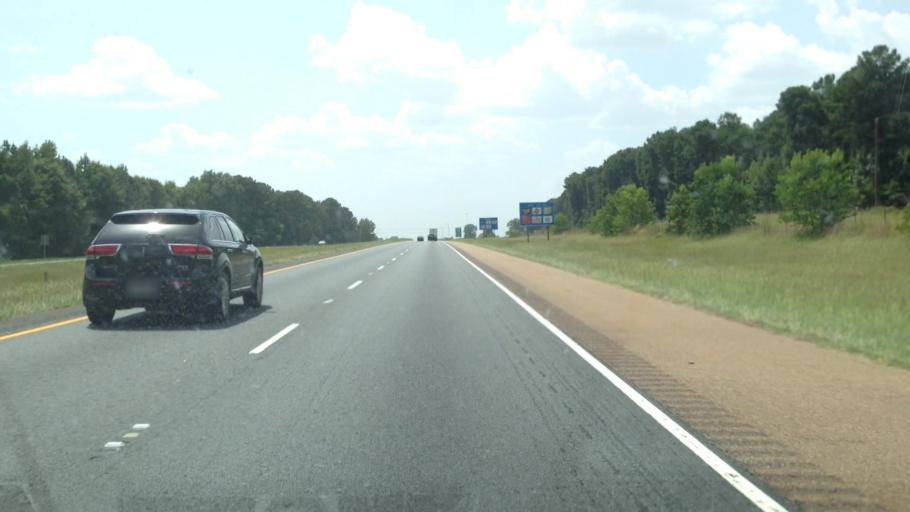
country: US
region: Louisiana
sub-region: Bienville Parish
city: Arcadia
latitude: 32.5615
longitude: -92.9001
